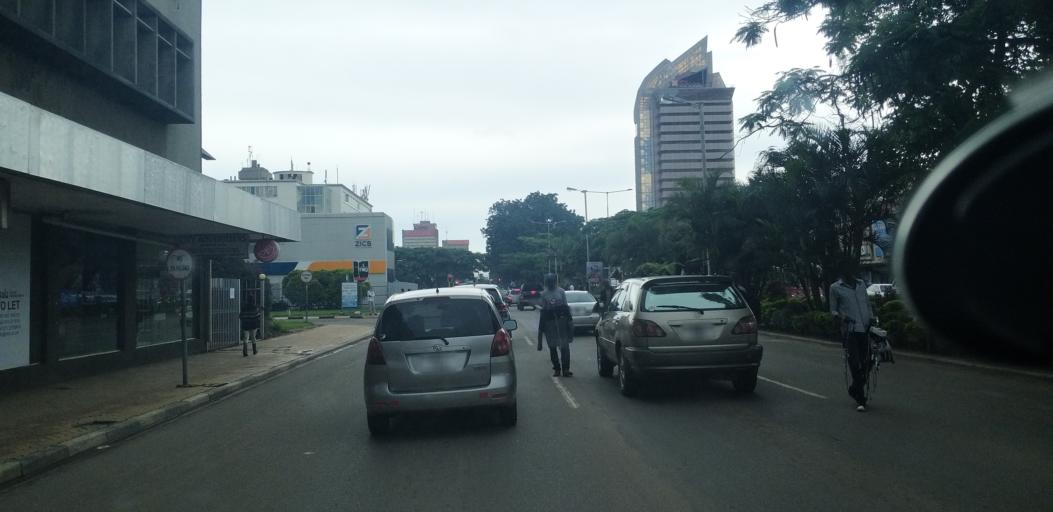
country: ZM
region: Lusaka
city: Lusaka
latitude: -15.4152
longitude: 28.2816
